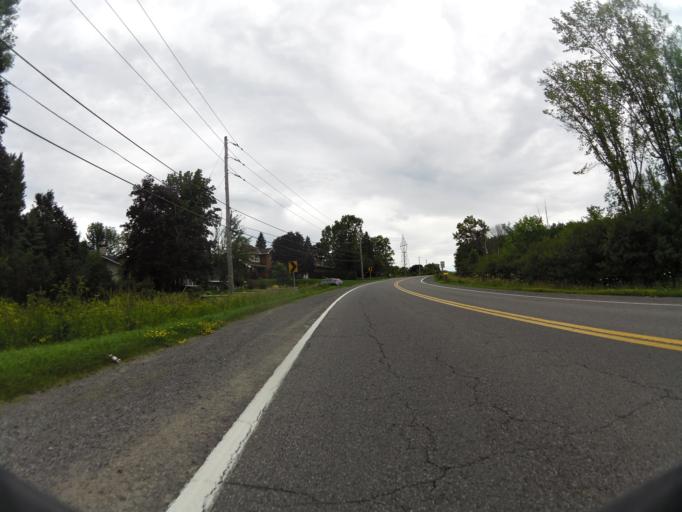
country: CA
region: Ontario
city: Ottawa
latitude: 45.2741
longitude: -75.6322
